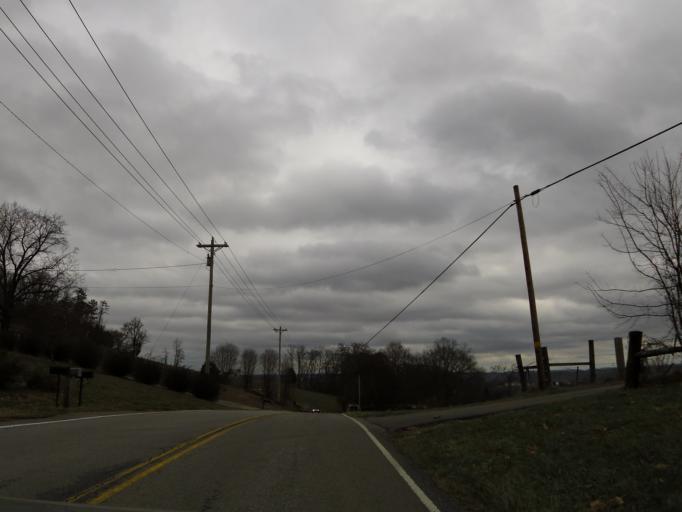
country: US
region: Tennessee
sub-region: Jefferson County
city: Jefferson City
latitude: 36.1899
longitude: -83.5068
